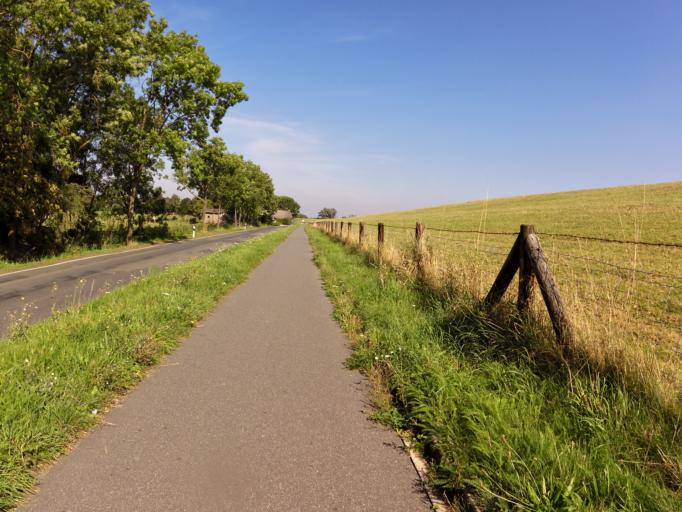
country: DE
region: Lower Saxony
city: Elsfleth
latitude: 53.2788
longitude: 8.4809
